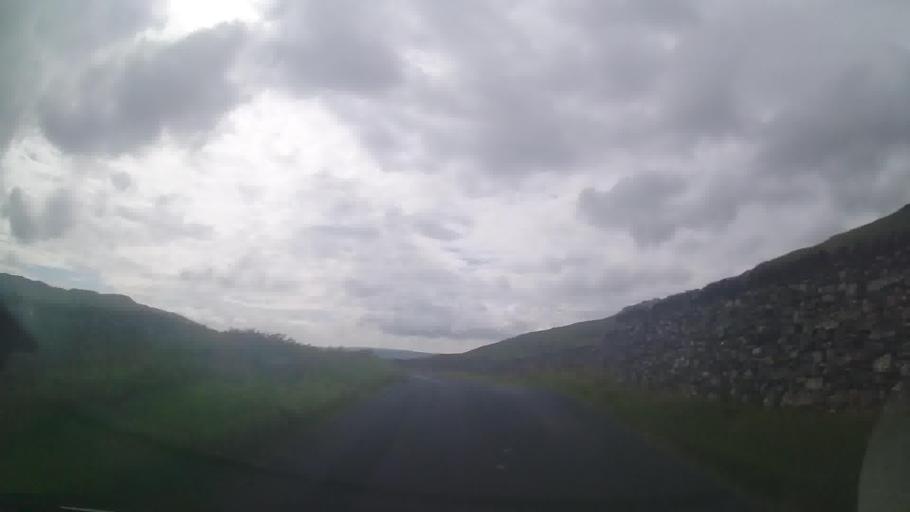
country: GB
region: England
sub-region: Cumbria
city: Ambleside
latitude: 54.4531
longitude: -2.9361
